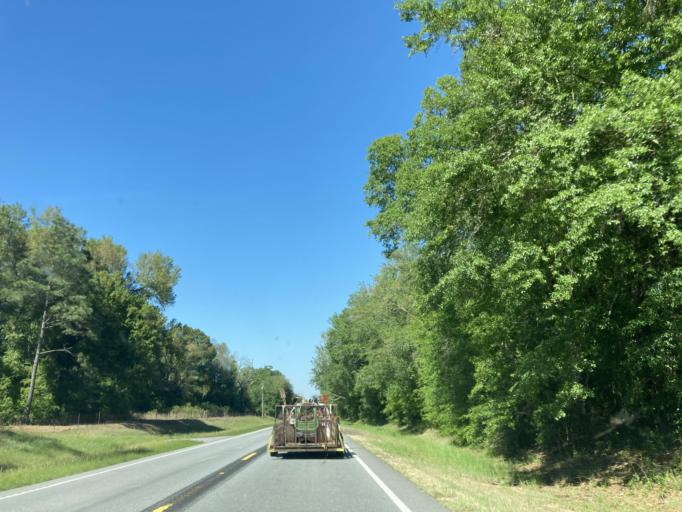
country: US
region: Georgia
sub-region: Baker County
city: Newton
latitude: 31.4375
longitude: -84.2737
